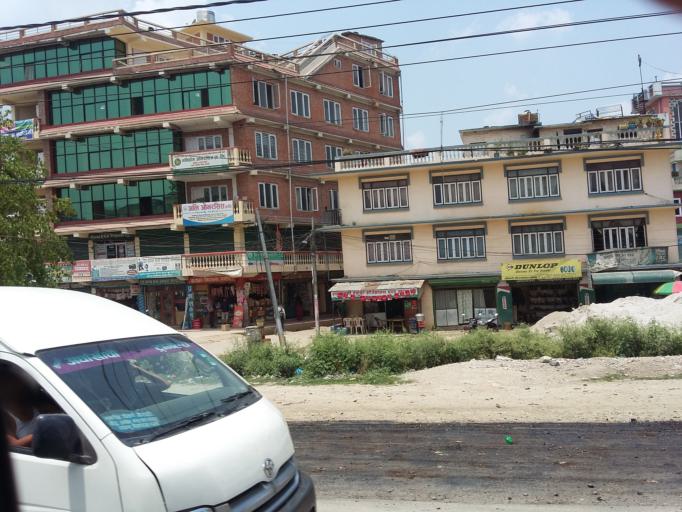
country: NP
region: Central Region
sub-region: Bagmati Zone
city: Kathmandu
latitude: 27.7365
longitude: 85.3224
